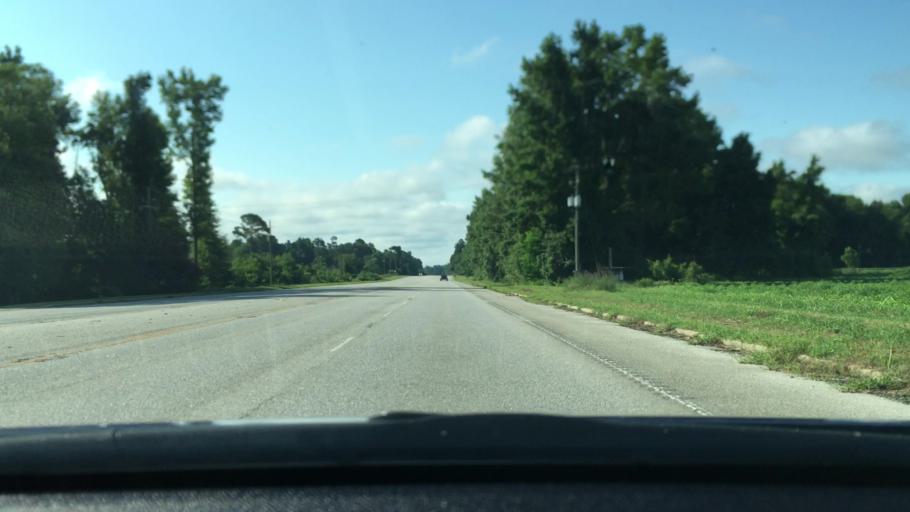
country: US
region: South Carolina
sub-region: Clarendon County
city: Manning
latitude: 33.7625
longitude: -80.2301
